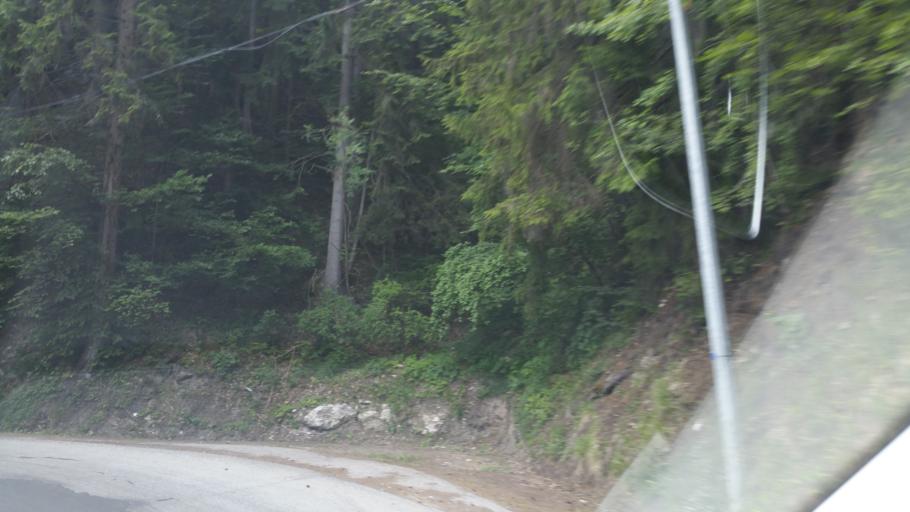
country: FR
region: Rhone-Alpes
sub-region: Departement de la Savoie
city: Saint-Jean-de-Maurienne
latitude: 45.2298
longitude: 6.3056
